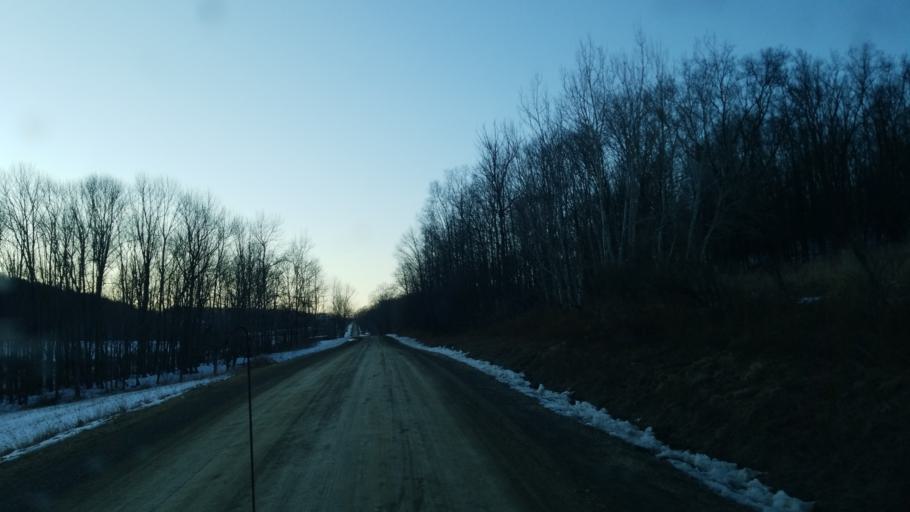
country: US
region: Pennsylvania
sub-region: Tioga County
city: Westfield
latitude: 42.0382
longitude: -77.5879
